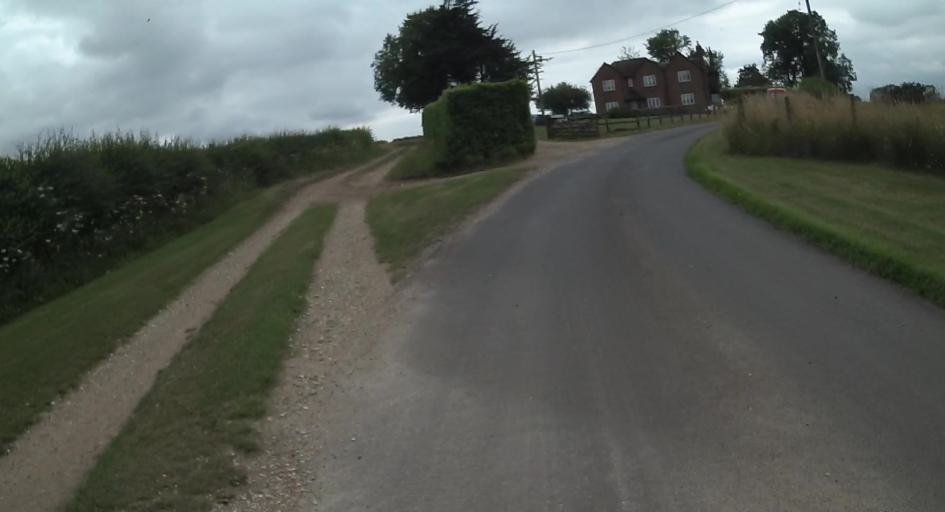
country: GB
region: England
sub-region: Hampshire
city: Swanmore
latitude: 51.0235
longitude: -1.1711
